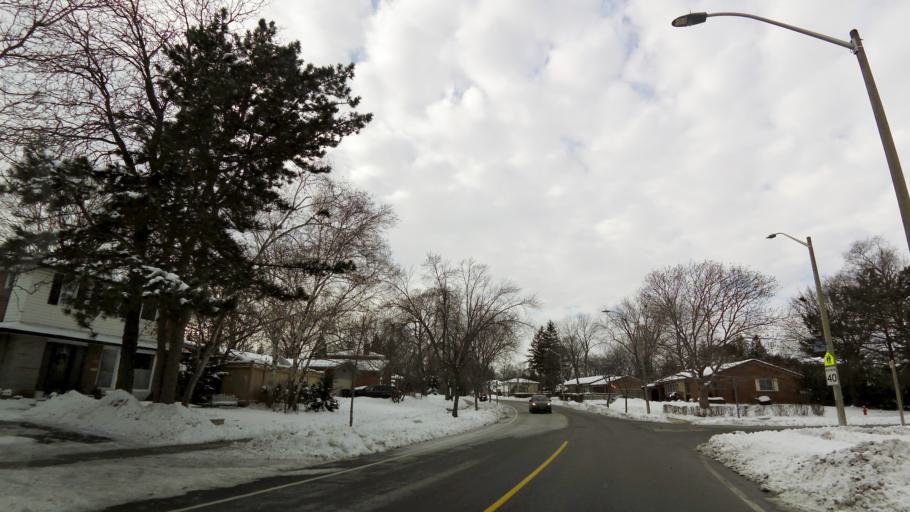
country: CA
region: Ontario
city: Mississauga
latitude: 43.5292
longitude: -79.6663
